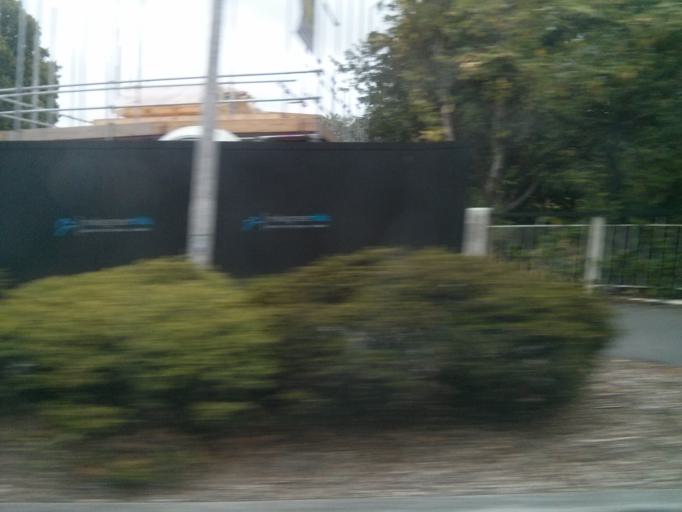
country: NZ
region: Canterbury
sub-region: Christchurch City
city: Christchurch
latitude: -43.5245
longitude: 172.6024
